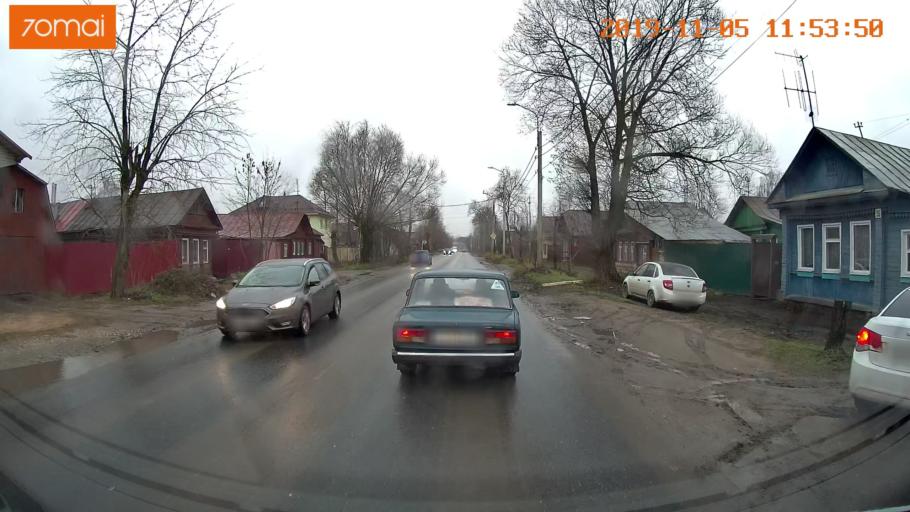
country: RU
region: Ivanovo
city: Bogorodskoye
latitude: 56.9943
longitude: 41.0306
